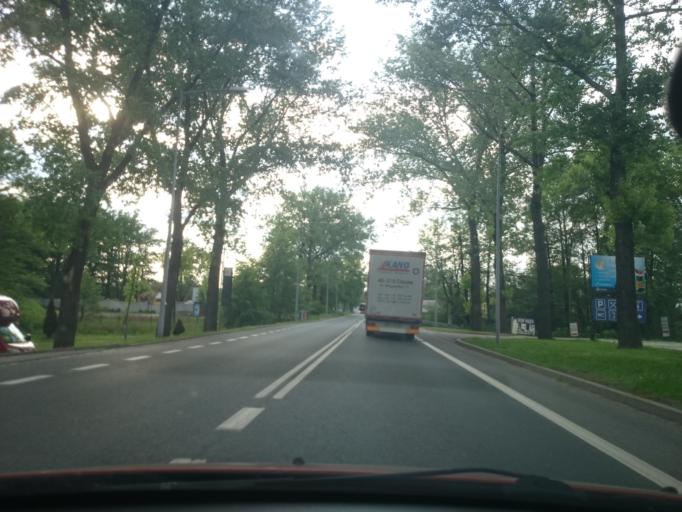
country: PL
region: Opole Voivodeship
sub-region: Powiat opolski
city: Opole
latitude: 50.6427
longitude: 17.9919
